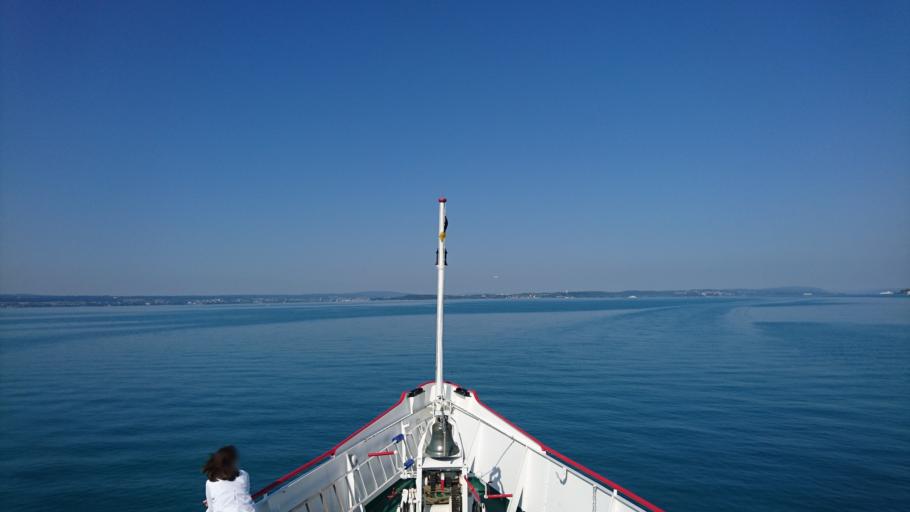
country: DE
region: Baden-Wuerttemberg
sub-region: Tuebingen Region
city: Hagnau
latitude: 47.6714
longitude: 9.3068
